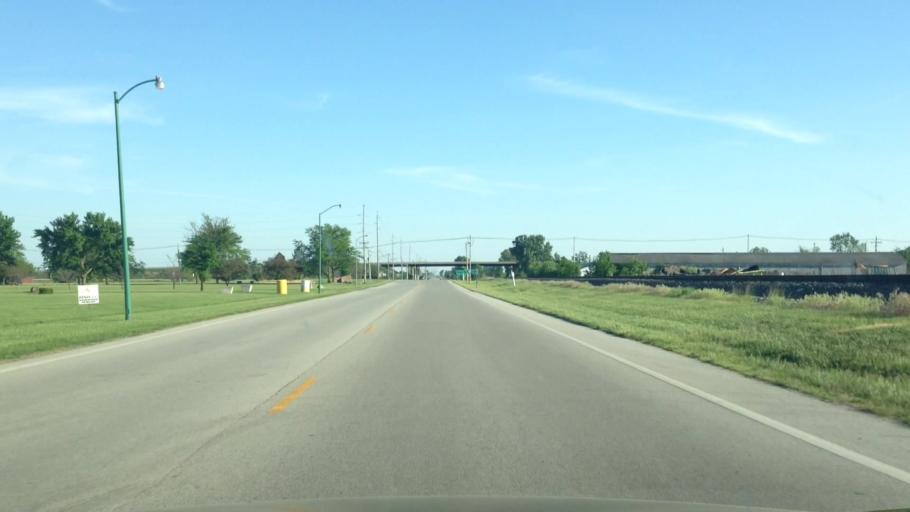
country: US
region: Ohio
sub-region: Auglaize County
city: Wapakoneta
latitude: 40.5606
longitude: -84.1942
